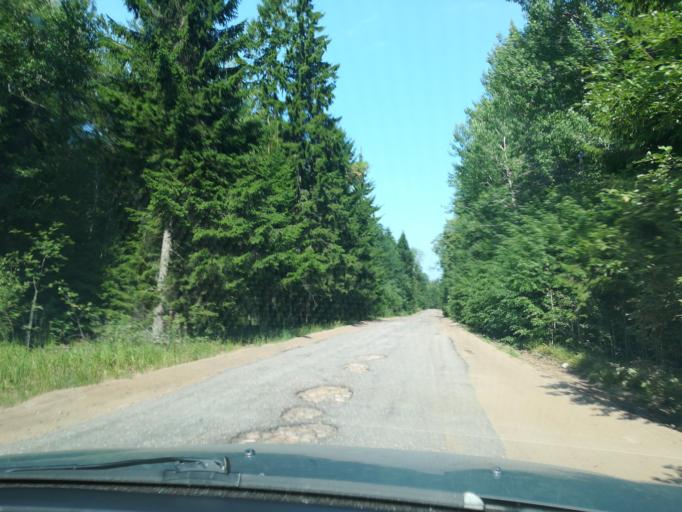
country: RU
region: Leningrad
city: Ust'-Luga
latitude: 59.7161
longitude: 28.2042
